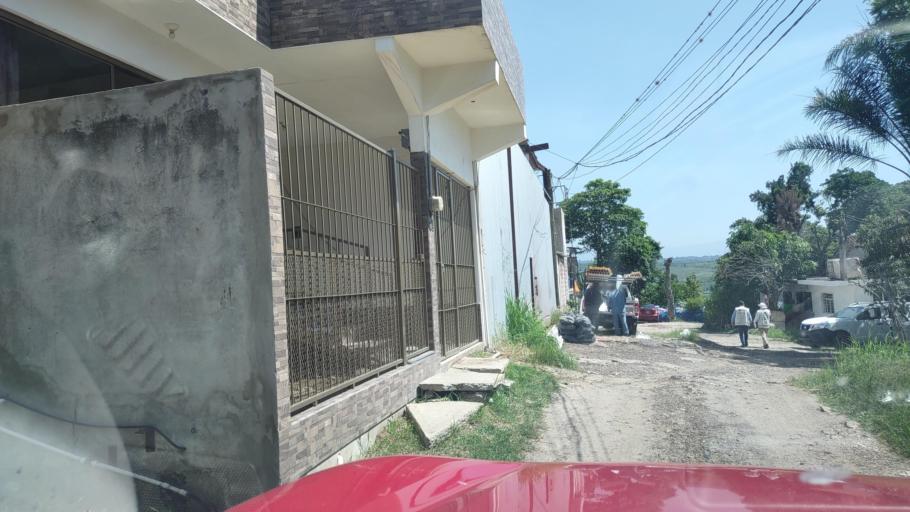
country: MX
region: Veracruz
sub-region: Emiliano Zapata
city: Dos Rios
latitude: 19.4905
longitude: -96.8151
